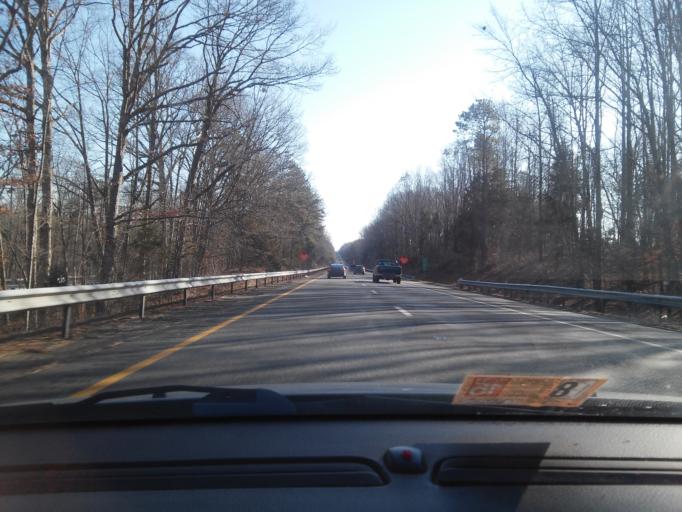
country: US
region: Virginia
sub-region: Henrico County
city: Wyndham
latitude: 37.6929
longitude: -77.7059
